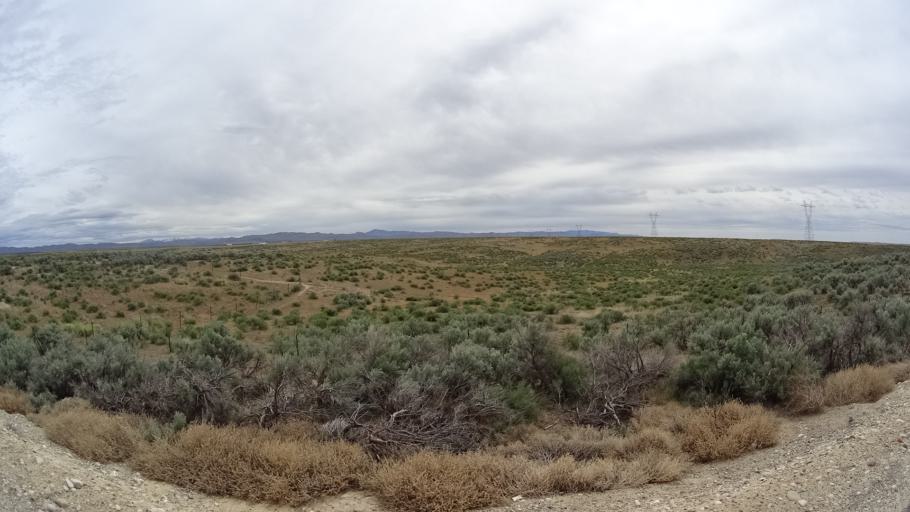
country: US
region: Idaho
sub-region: Ada County
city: Boise
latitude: 43.3747
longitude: -116.0049
